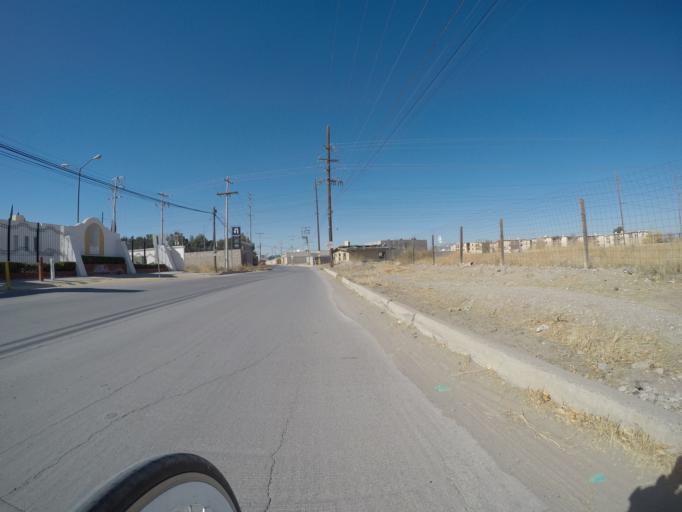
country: MX
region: Chihuahua
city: Ciudad Juarez
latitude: 31.6950
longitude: -106.4001
